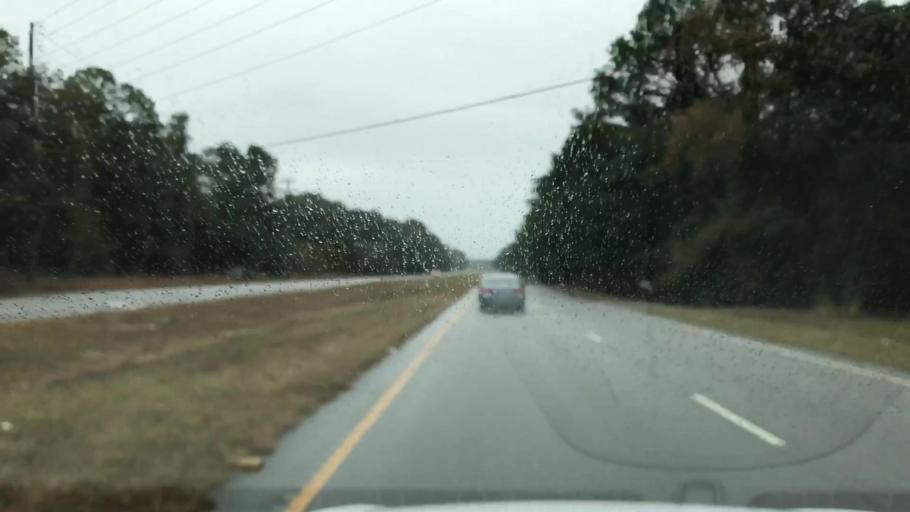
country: US
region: South Carolina
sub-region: Charleston County
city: Isle of Palms
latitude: 32.8902
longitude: -79.7406
